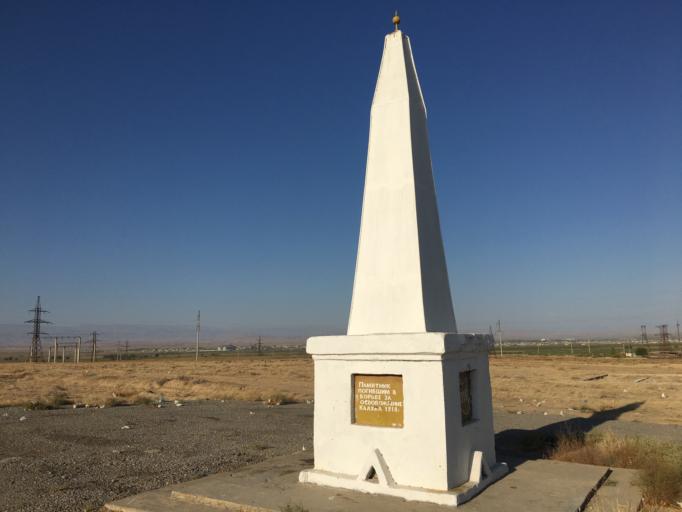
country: TM
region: Ahal
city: Kaka
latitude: 37.3463
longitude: 59.6724
